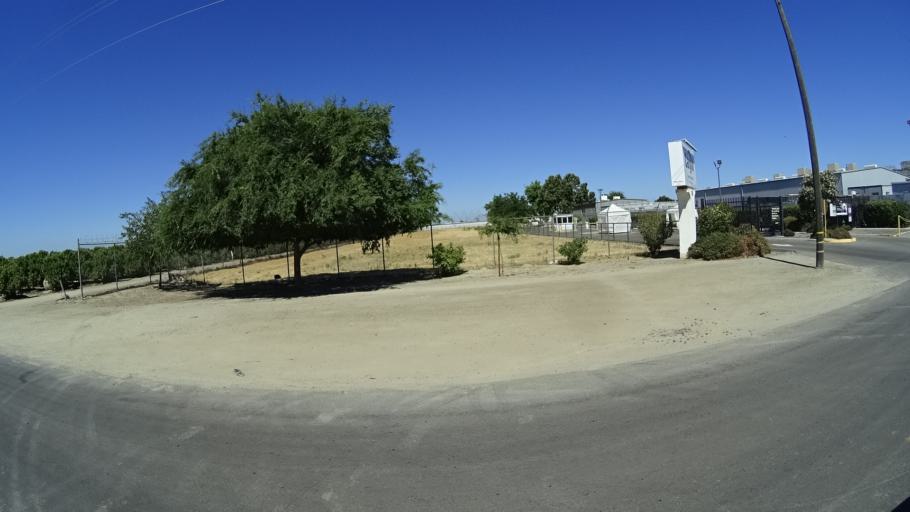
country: US
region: California
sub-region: Fresno County
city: Easton
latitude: 36.6869
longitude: -119.7998
